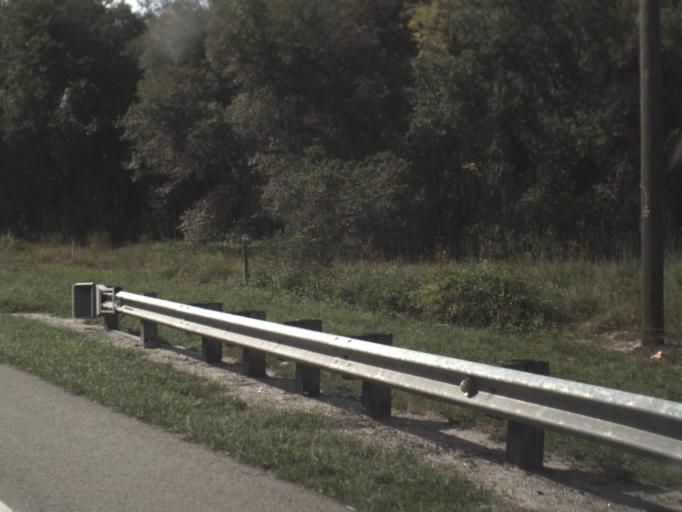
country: US
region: Florida
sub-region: Sarasota County
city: The Meadows
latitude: 27.4741
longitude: -82.2669
